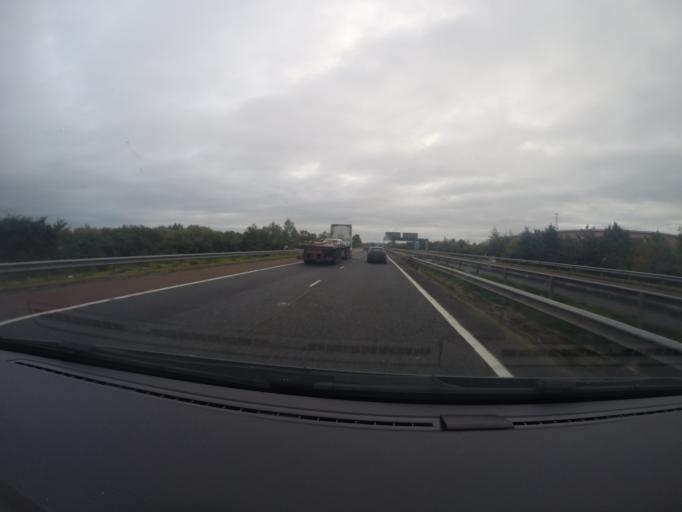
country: GB
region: Northern Ireland
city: Hillsborough
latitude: 54.4924
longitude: -6.0729
